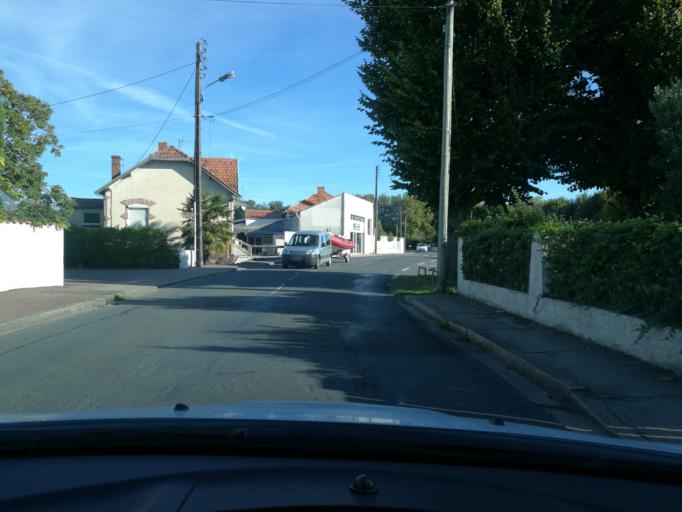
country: FR
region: Poitou-Charentes
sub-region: Departement de la Charente-Maritime
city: Saint-Trojan-les-Bains
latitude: 45.8865
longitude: -1.2010
